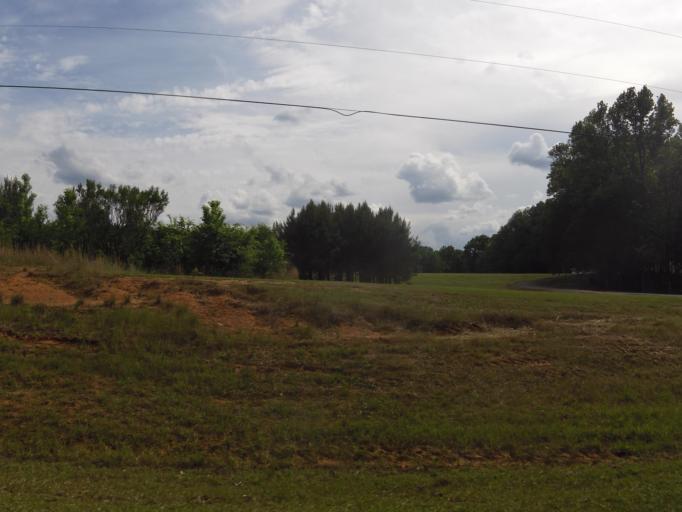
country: US
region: Georgia
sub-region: McDuffie County
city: Thomson
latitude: 33.5298
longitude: -82.4818
